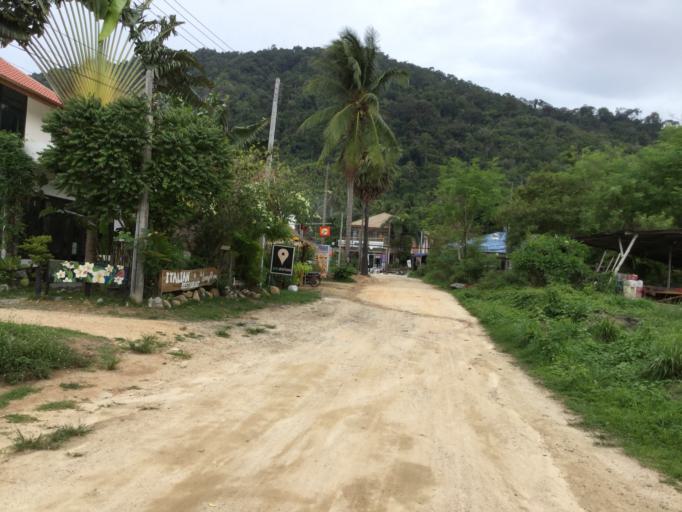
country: TH
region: Nakhon Si Thammarat
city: Ko Pha Ngan
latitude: 9.7698
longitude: 100.0565
